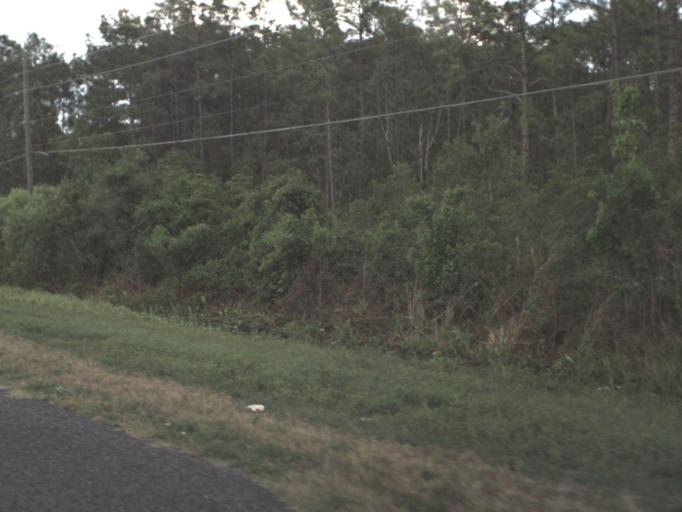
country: US
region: Florida
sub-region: Lake County
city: Eustis
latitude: 28.8823
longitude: -81.6872
